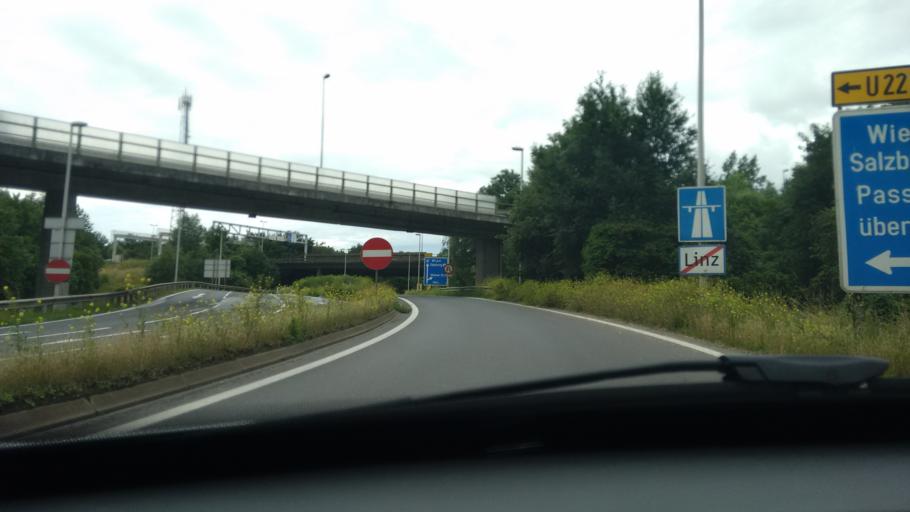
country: AT
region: Upper Austria
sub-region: Linz Stadt
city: Linz
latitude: 48.2861
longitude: 14.3183
